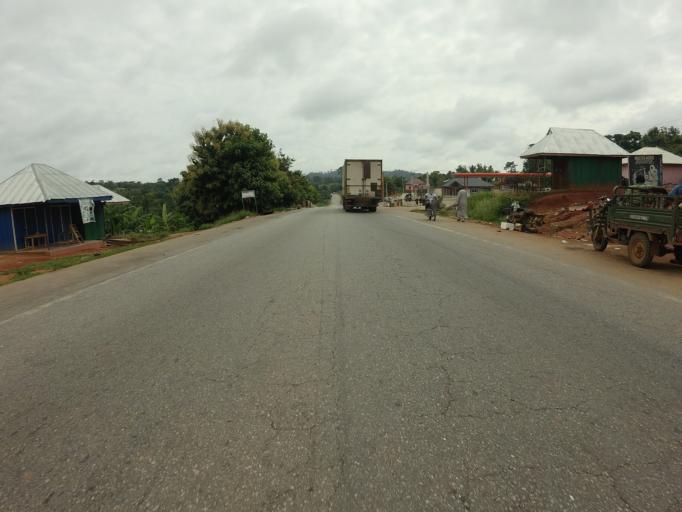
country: GH
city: Bechem
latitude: 7.1376
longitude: -1.7352
